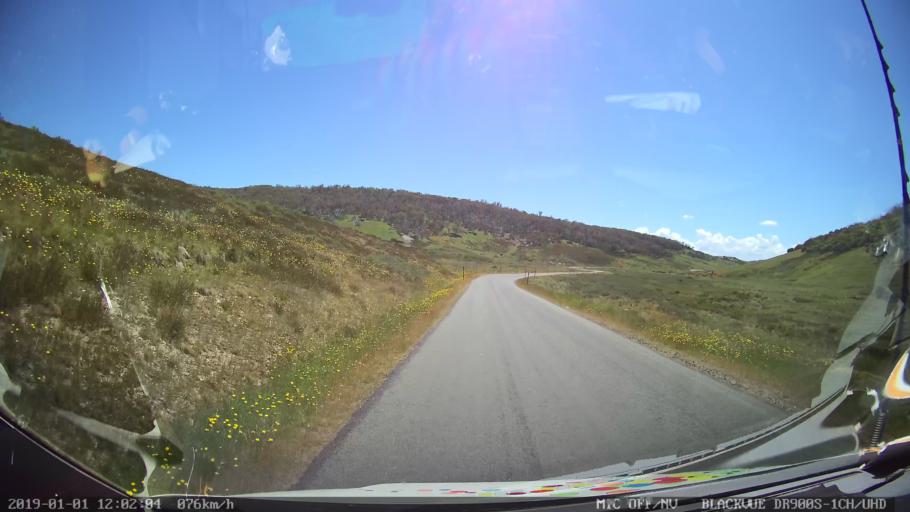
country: AU
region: New South Wales
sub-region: Snowy River
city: Jindabyne
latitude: -35.8752
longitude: 148.4736
